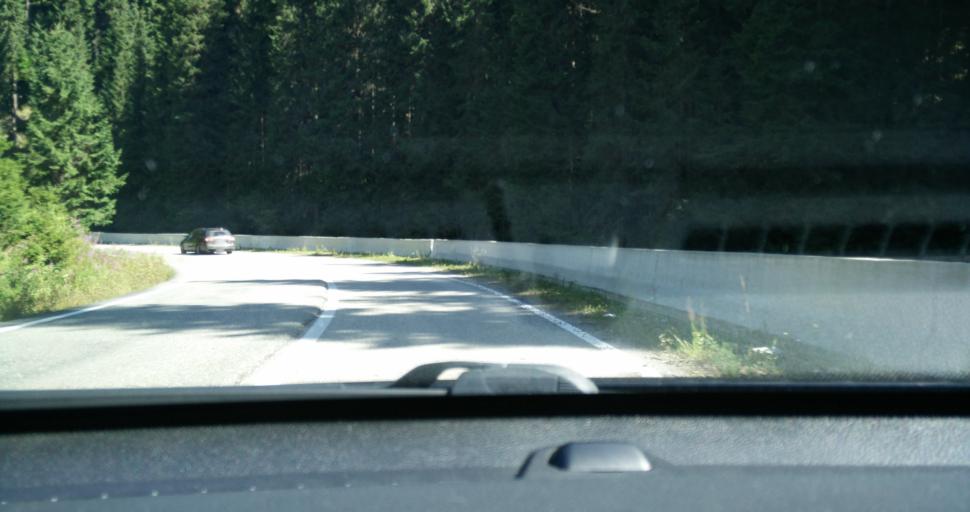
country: RO
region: Hunedoara
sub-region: Oras Petrila
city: Petrila
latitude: 45.5191
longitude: 23.6523
